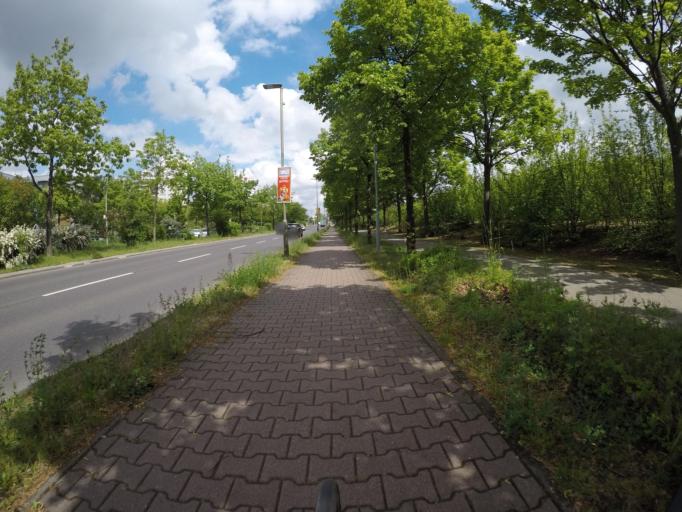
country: DE
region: Berlin
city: Marzahn
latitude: 52.5363
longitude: 13.5677
